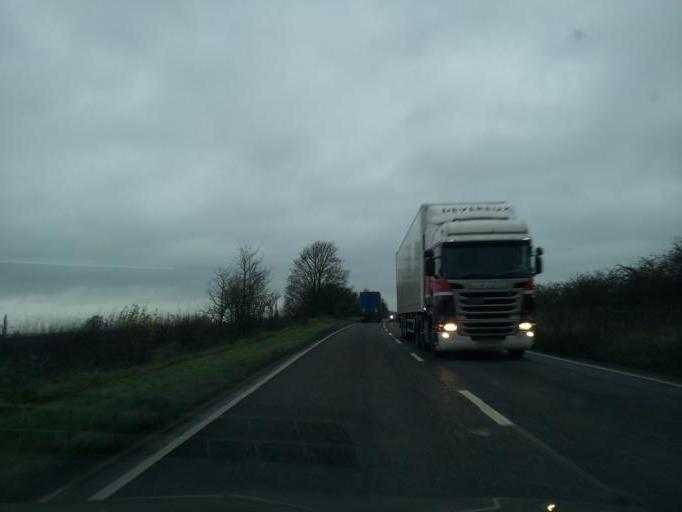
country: GB
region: England
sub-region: Northamptonshire
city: Daventry
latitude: 52.3426
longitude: -1.1745
